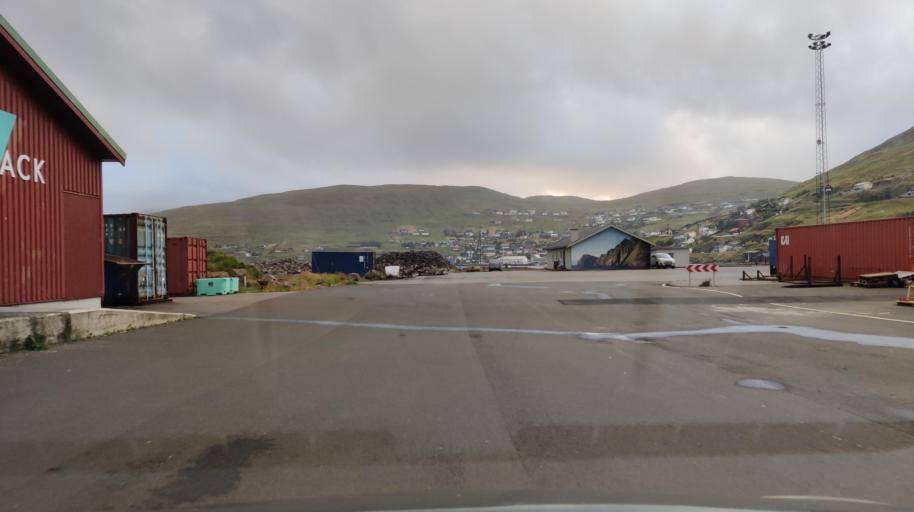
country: FO
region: Streymoy
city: Vestmanna
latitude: 62.1519
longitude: -7.1477
